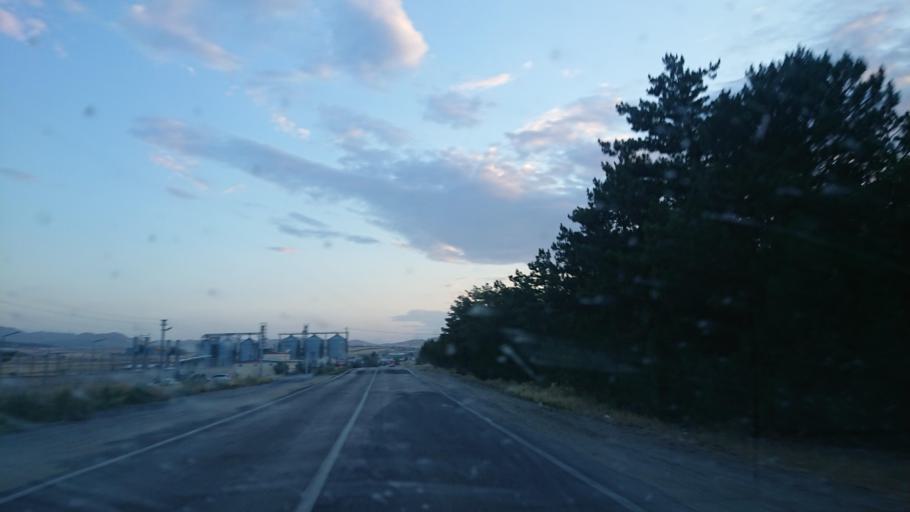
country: TR
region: Aksaray
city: Balci
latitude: 38.7640
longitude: 34.0908
